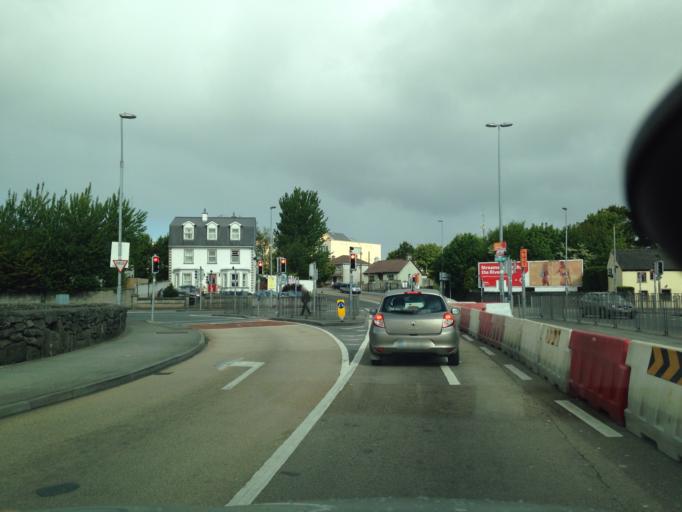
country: IE
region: Connaught
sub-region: County Galway
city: Gaillimh
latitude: 53.2819
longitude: -9.0331
